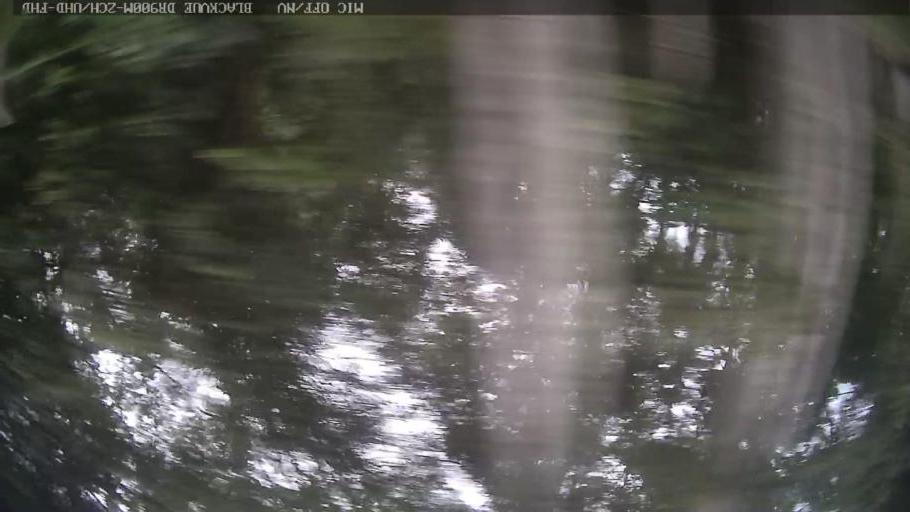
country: BR
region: Sao Paulo
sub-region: Rio Grande Da Serra
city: Rio Grande da Serra
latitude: -23.6874
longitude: -46.3043
